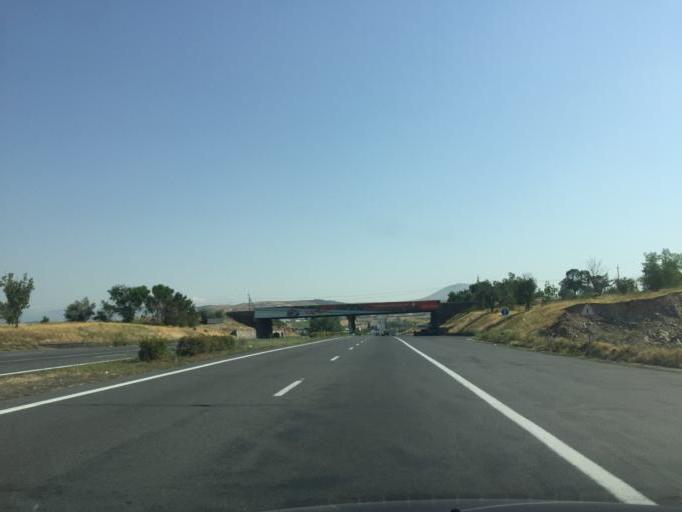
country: AM
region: Kotayk'i Marz
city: Arzni
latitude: 40.2839
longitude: 44.6055
